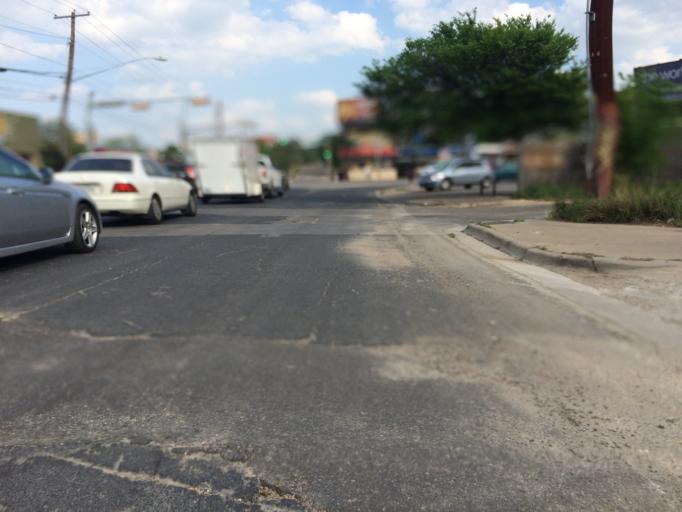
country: US
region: Texas
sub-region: Travis County
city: Austin
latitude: 30.2957
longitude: -97.7433
